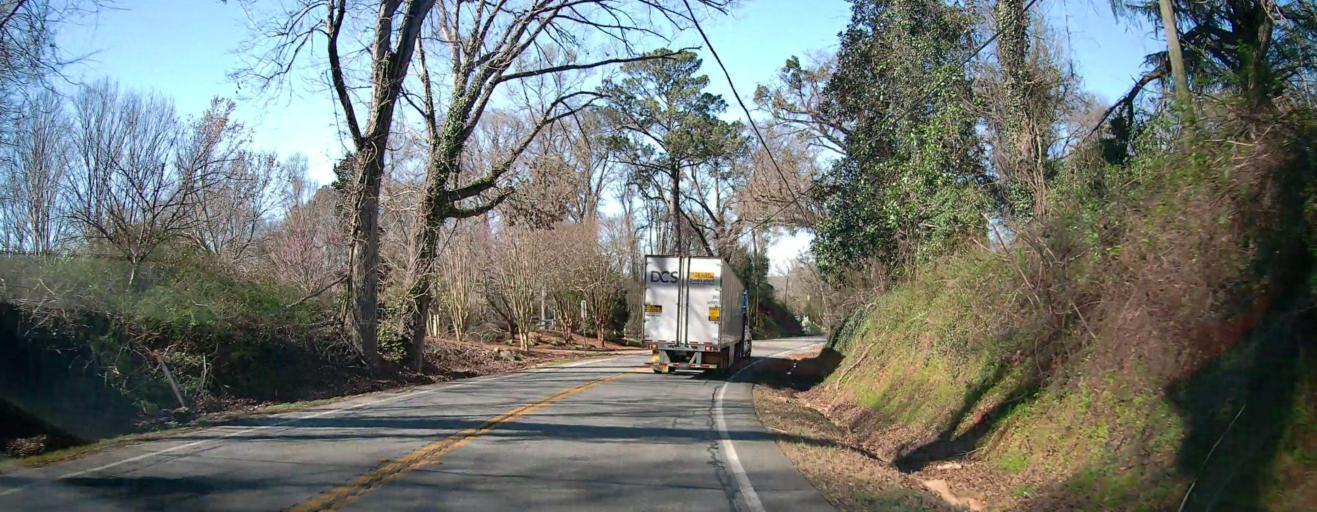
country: US
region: Georgia
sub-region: Butts County
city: Indian Springs
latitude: 33.2393
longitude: -83.9211
